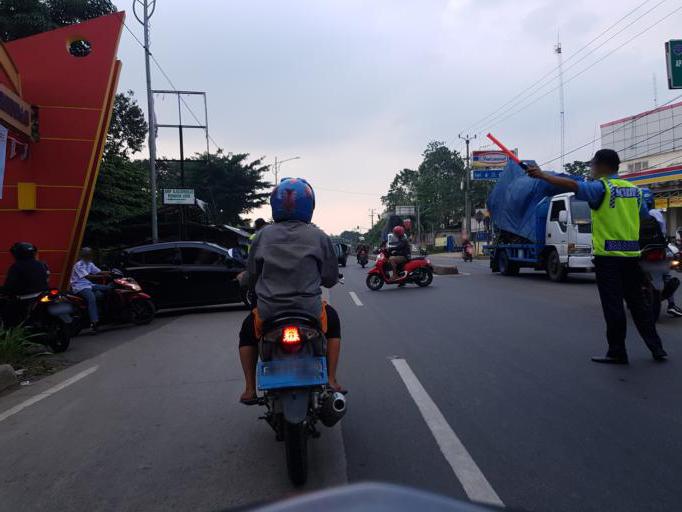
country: ID
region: West Java
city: Parung
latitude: -6.4918
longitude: 106.7424
